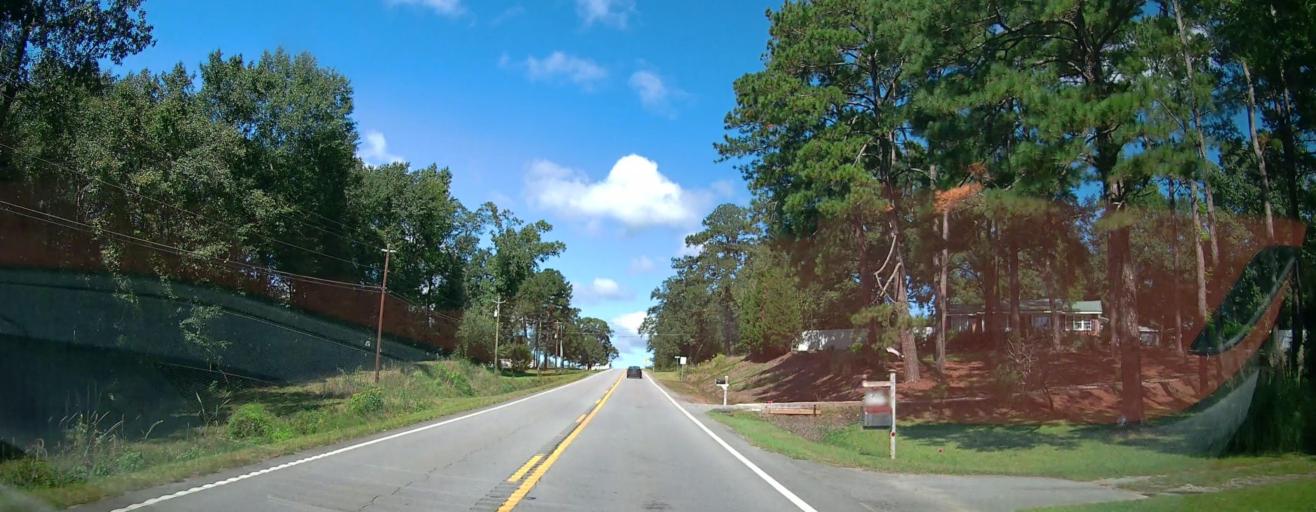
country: US
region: Georgia
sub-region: Bibb County
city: Macon
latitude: 32.8192
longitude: -83.5700
